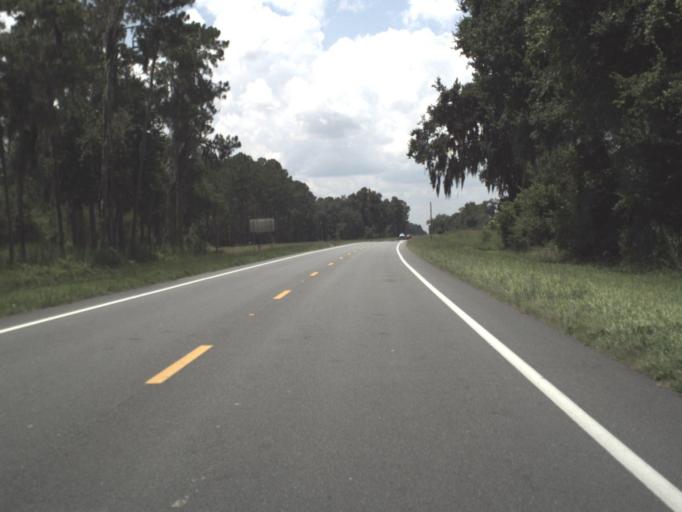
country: US
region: Florida
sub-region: Suwannee County
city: Wellborn
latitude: 30.3885
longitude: -82.8230
